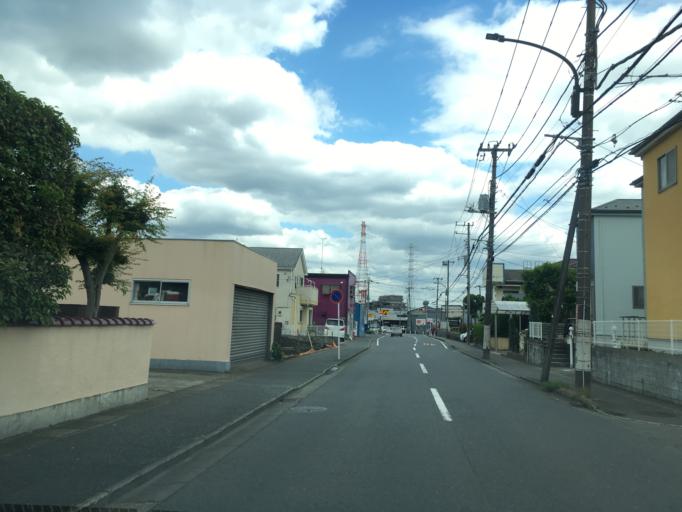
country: JP
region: Tokyo
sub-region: Machida-shi
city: Machida
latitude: 35.5622
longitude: 139.4040
